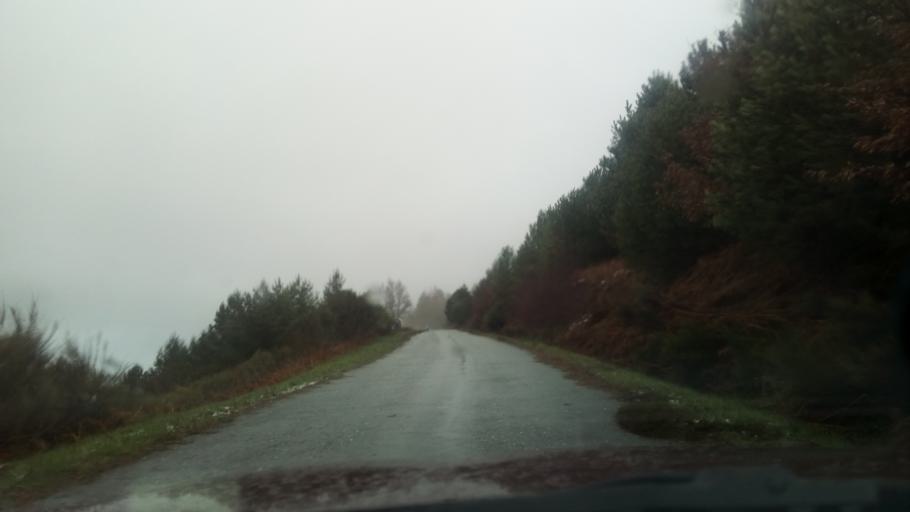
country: PT
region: Guarda
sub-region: Celorico da Beira
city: Celorico da Beira
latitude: 40.5289
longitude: -7.4507
